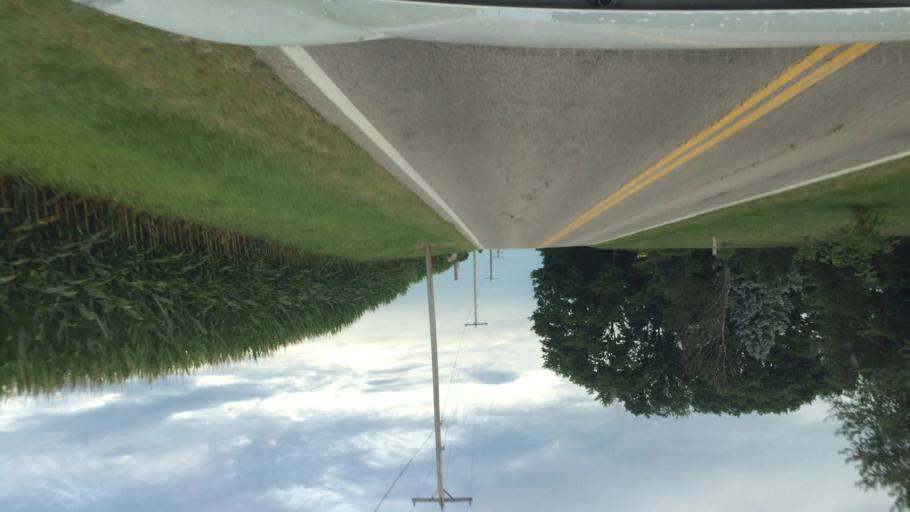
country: US
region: Ohio
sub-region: Clark County
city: Lisbon
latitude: 39.9429
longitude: -83.6315
